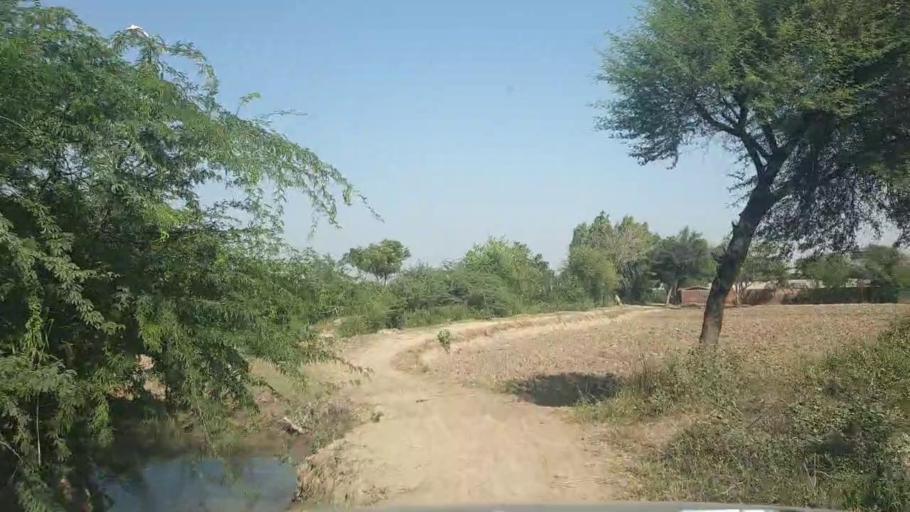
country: PK
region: Sindh
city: Badin
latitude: 24.6815
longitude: 68.8933
